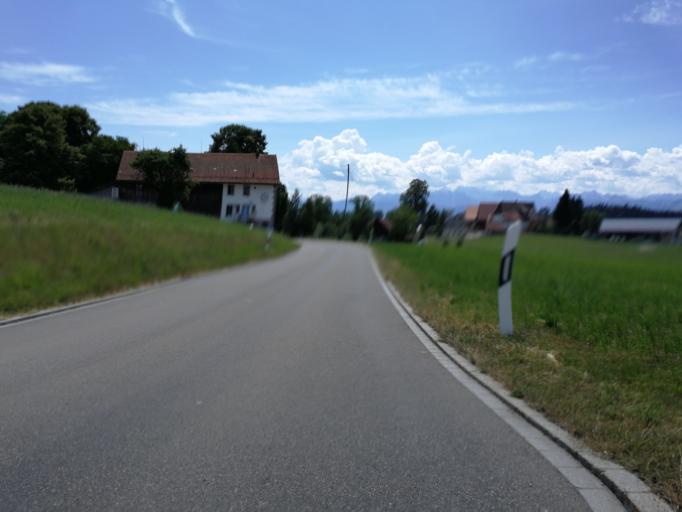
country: CH
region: Zurich
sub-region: Bezirk Hinwil
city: Wetzikon / Kempten
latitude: 47.3133
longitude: 8.8223
